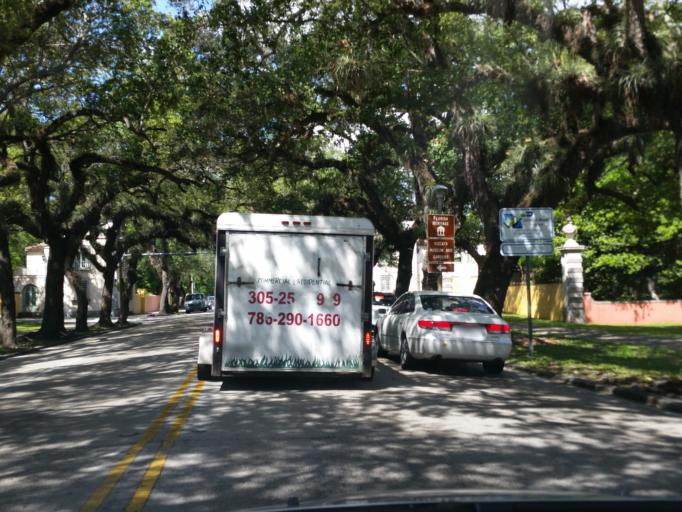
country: US
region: Florida
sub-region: Miami-Dade County
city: Miami
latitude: 25.7476
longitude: -80.2102
